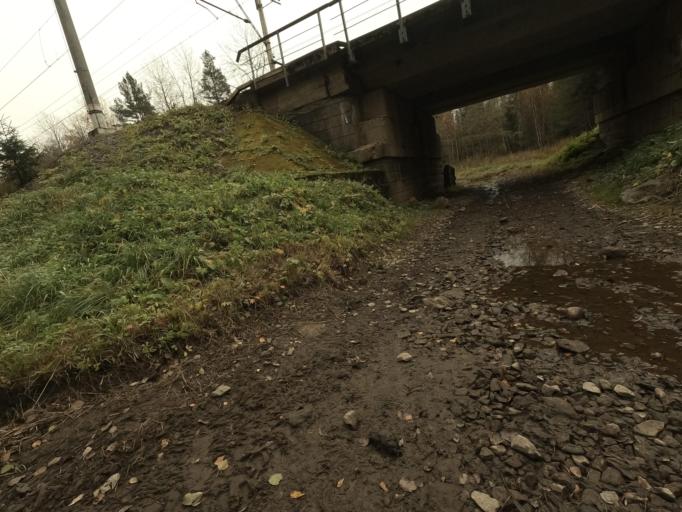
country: RU
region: Leningrad
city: Pavlovo
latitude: 59.7712
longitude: 30.9123
